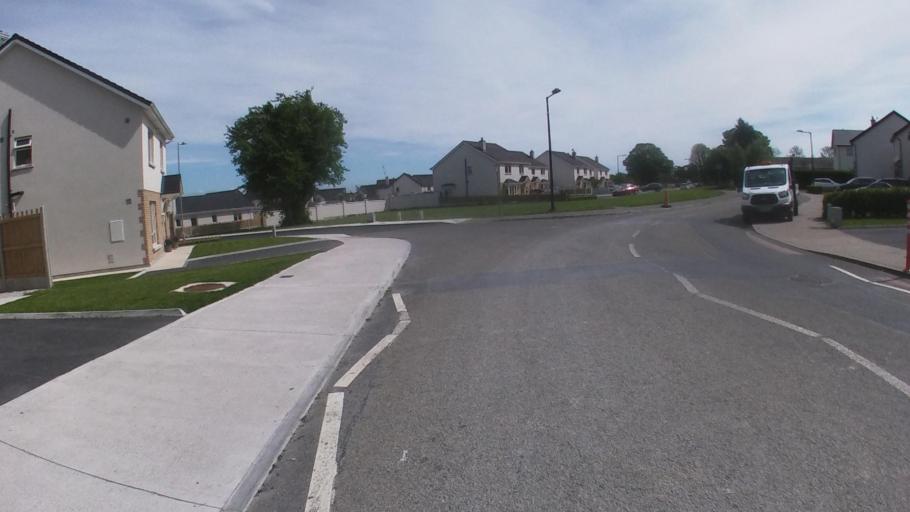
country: IE
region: Leinster
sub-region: County Carlow
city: Carlow
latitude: 52.8508
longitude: -6.9940
